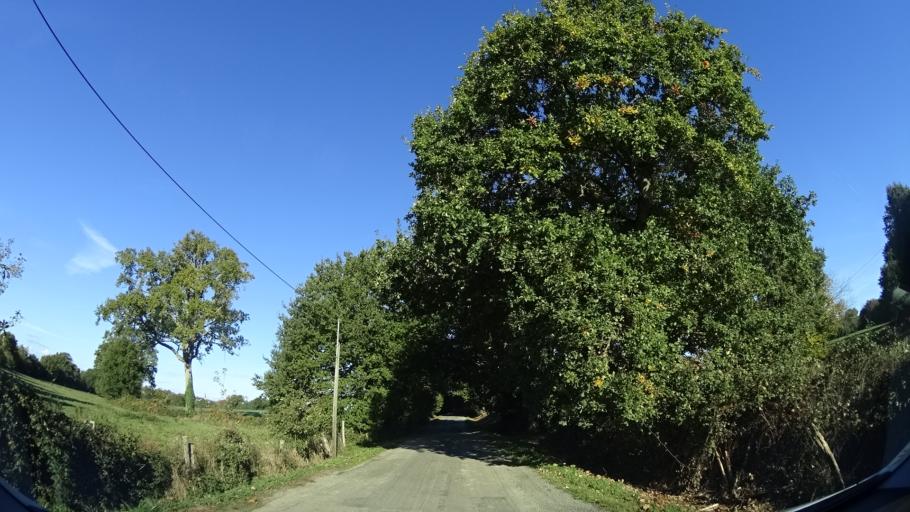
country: FR
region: Brittany
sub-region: Departement d'Ille-et-Vilaine
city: Geveze
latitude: 48.2118
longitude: -1.7750
